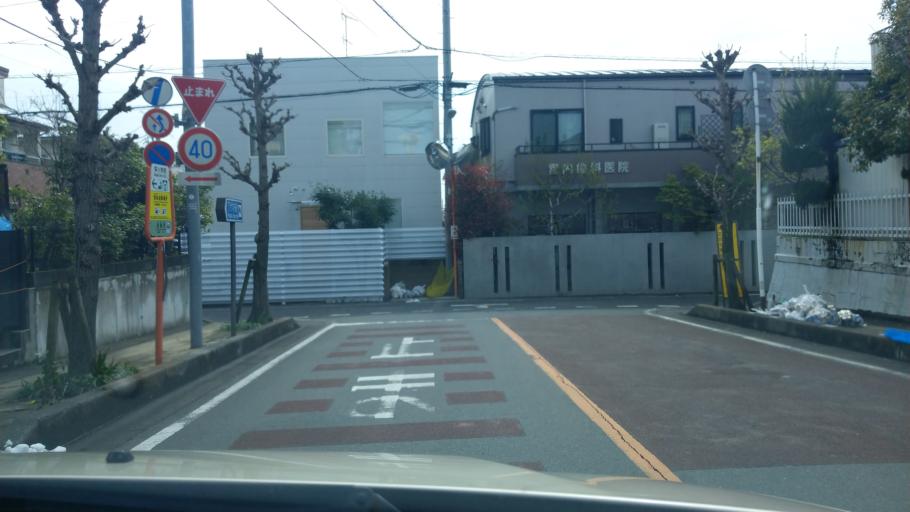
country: JP
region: Saitama
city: Yono
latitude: 35.9043
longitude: 139.5829
